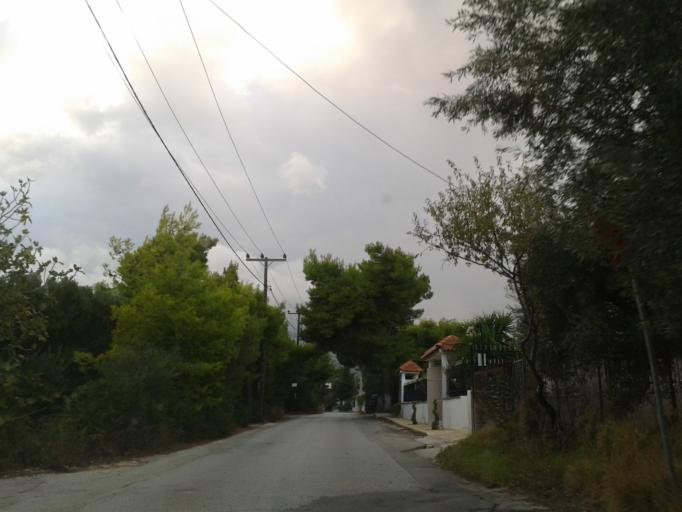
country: GR
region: Attica
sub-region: Nomarchia Anatolikis Attikis
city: Nea Makri
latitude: 38.0675
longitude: 23.9868
